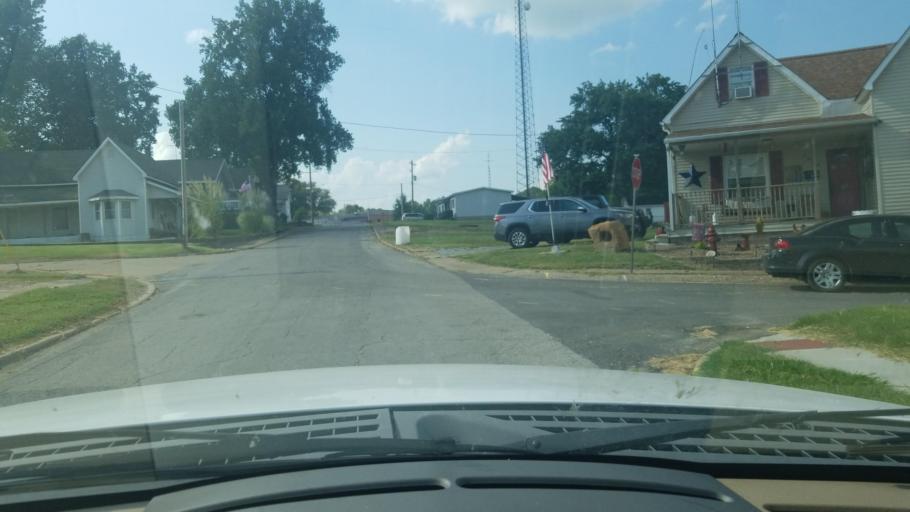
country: US
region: Illinois
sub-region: Saline County
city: Eldorado
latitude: 37.8151
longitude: -88.4434
